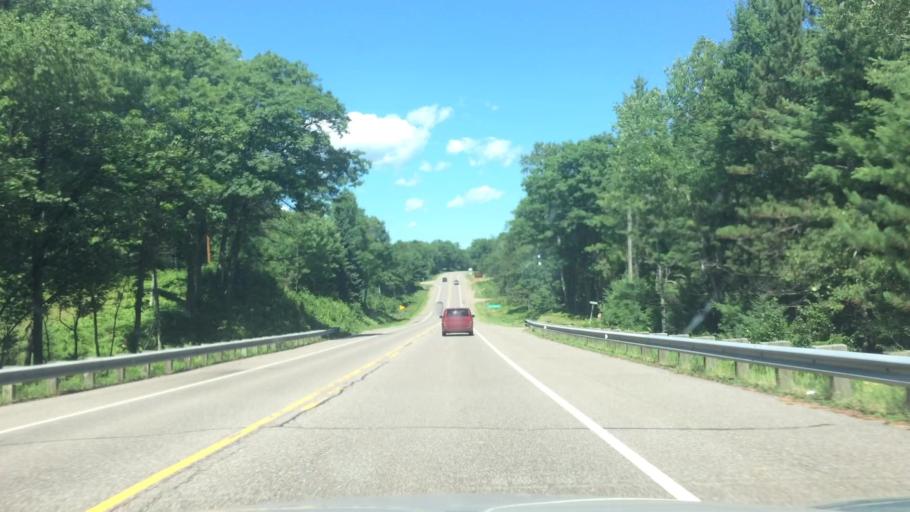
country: US
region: Wisconsin
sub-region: Vilas County
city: Lac du Flambeau
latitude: 45.7751
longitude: -89.7156
